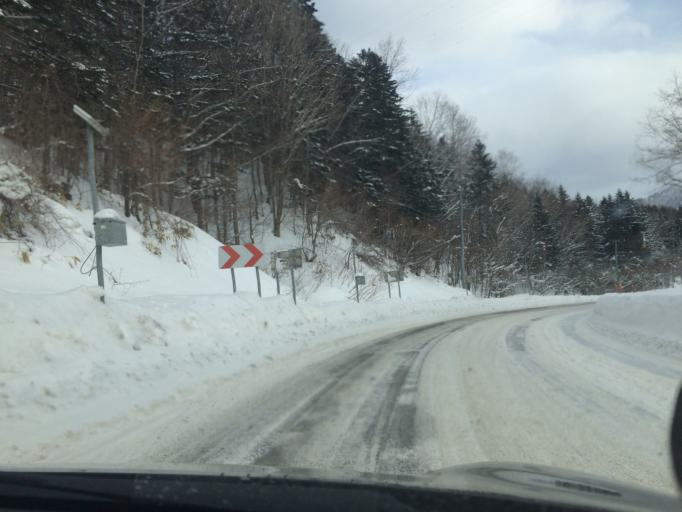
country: JP
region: Hokkaido
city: Shimo-furano
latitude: 43.0491
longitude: 142.5122
